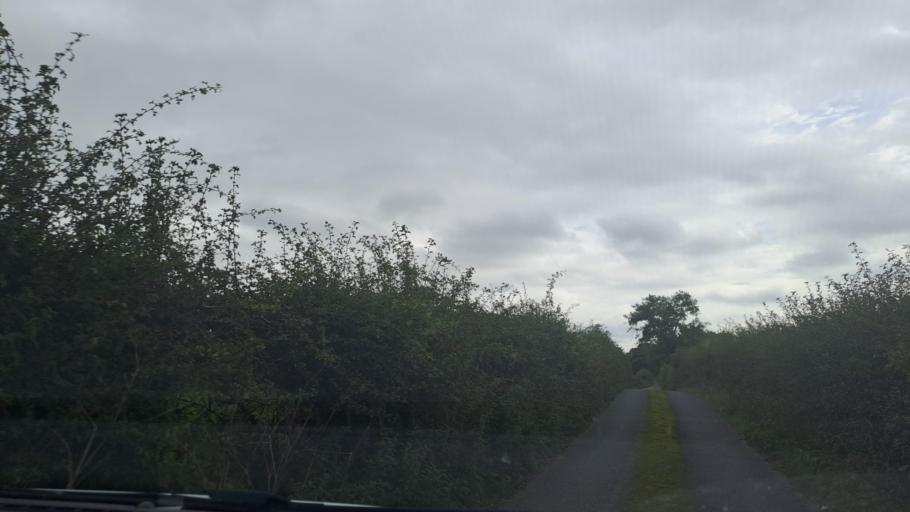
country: IE
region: Ulster
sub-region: An Cabhan
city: Kingscourt
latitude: 53.9740
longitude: -6.8506
